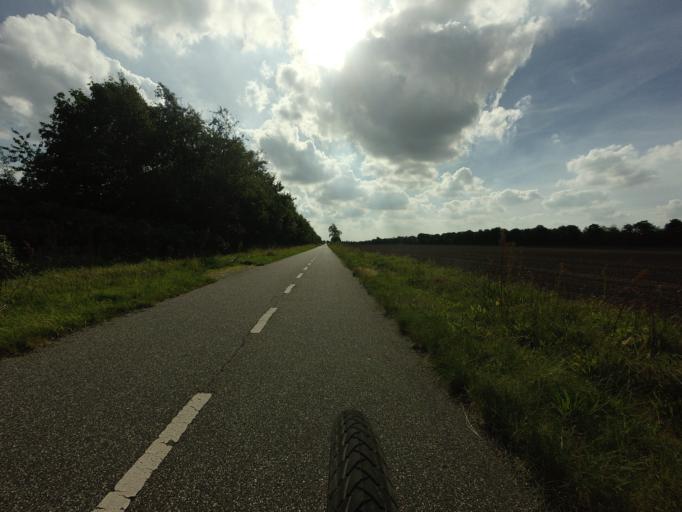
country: DK
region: Central Jutland
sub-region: Herning Kommune
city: Sunds
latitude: 56.1944
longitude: 9.0138
